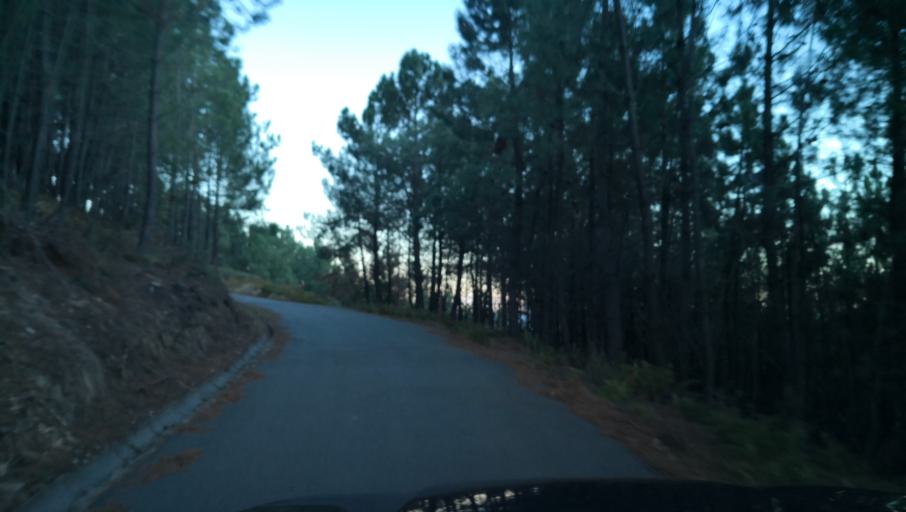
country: PT
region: Vila Real
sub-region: Santa Marta de Penaguiao
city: Santa Marta de Penaguiao
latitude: 41.2692
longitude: -7.8246
